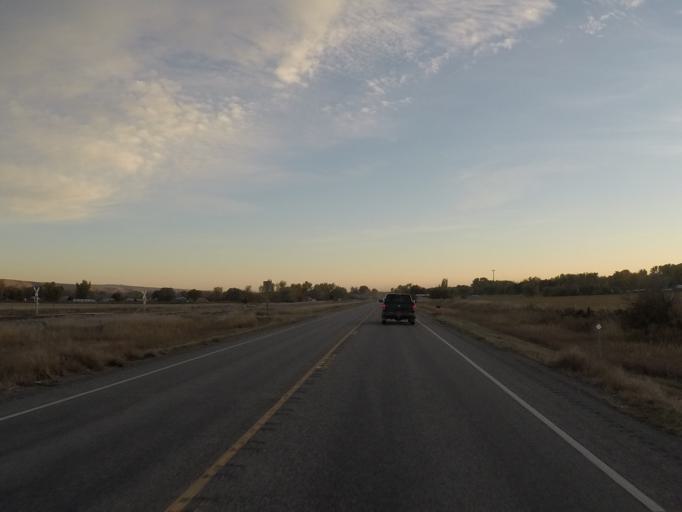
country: US
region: Montana
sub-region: Yellowstone County
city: Laurel
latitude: 45.5616
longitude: -108.8397
